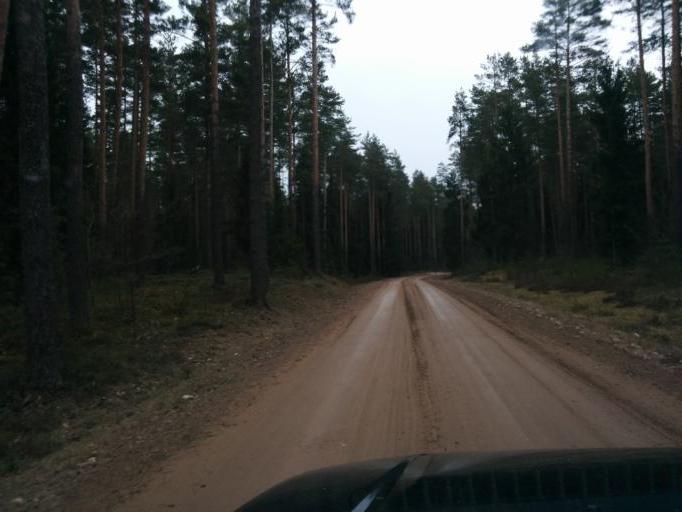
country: LV
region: Ogre
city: Ogre
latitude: 56.7811
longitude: 24.6067
